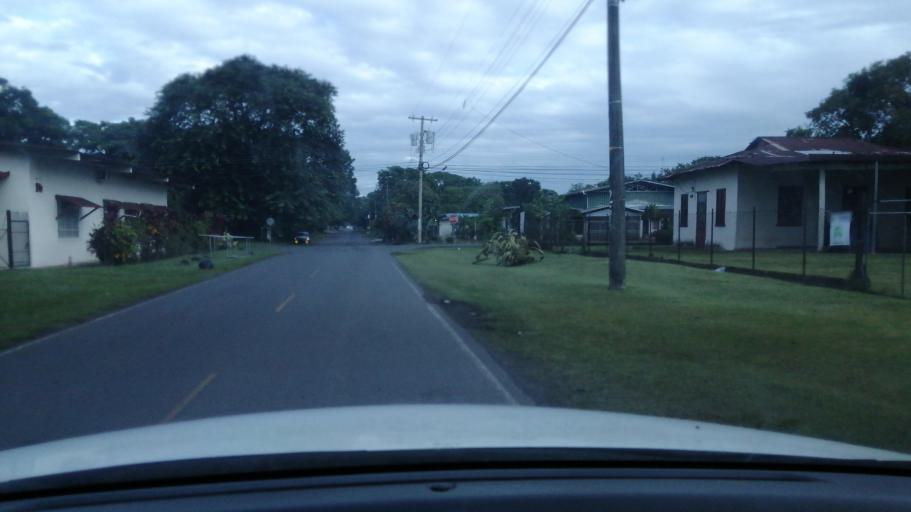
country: PA
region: Chiriqui
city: David
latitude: 8.4293
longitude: -82.4359
